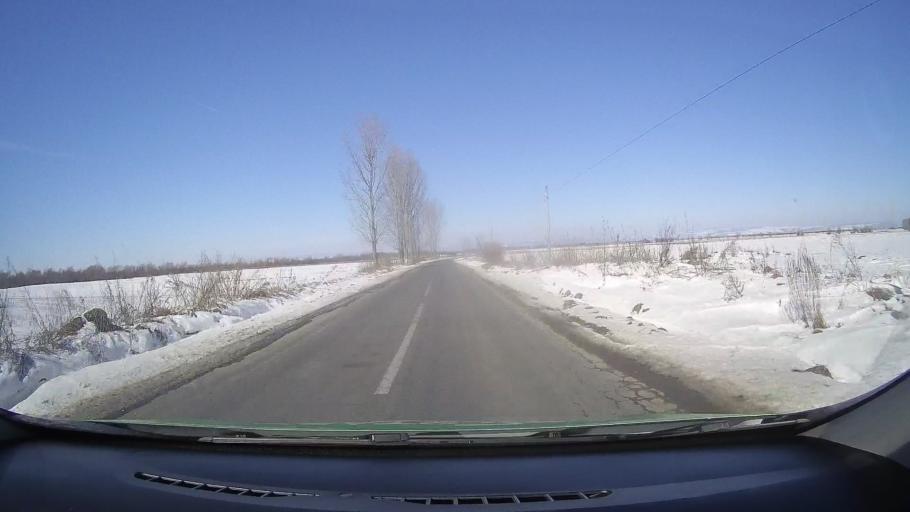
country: RO
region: Brasov
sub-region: Comuna Harseni
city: Harseni
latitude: 45.7330
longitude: 25.0269
